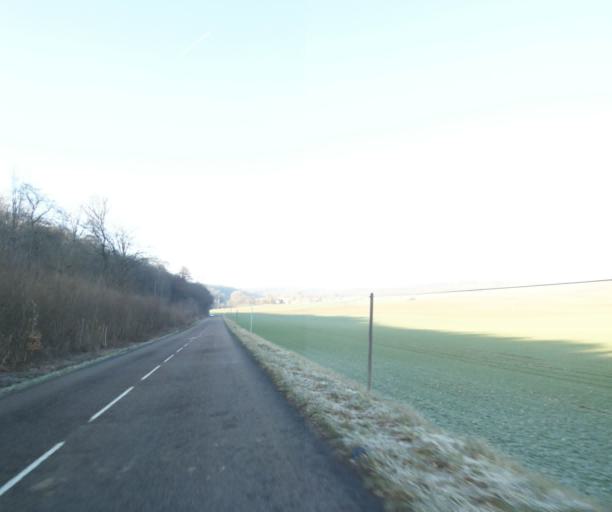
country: FR
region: Champagne-Ardenne
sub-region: Departement de la Haute-Marne
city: Chevillon
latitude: 48.5508
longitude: 5.0938
